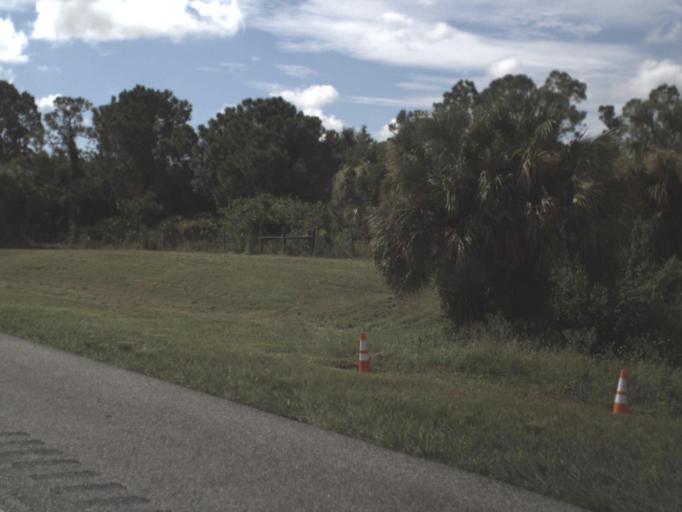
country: US
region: Florida
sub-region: Charlotte County
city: Port Charlotte
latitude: 27.0683
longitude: -82.0947
